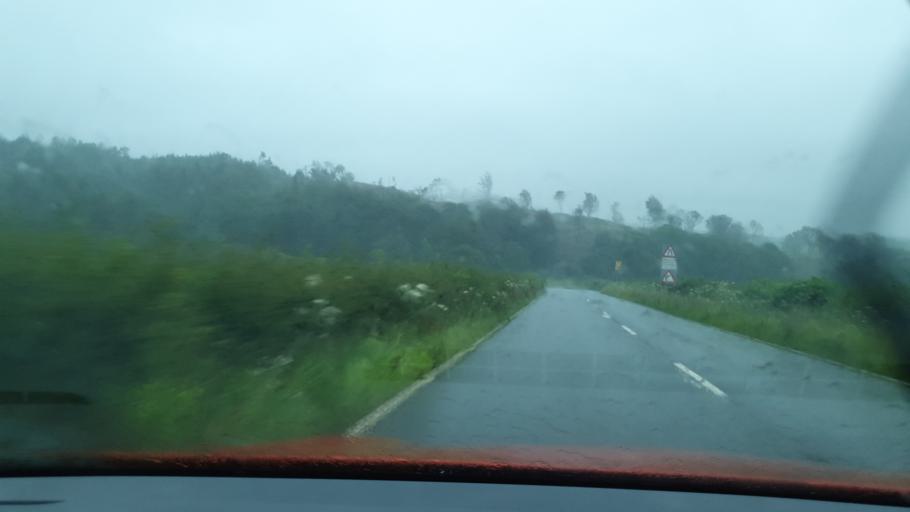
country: GB
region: England
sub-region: Cumbria
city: Askam in Furness
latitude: 54.2667
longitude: -3.1842
